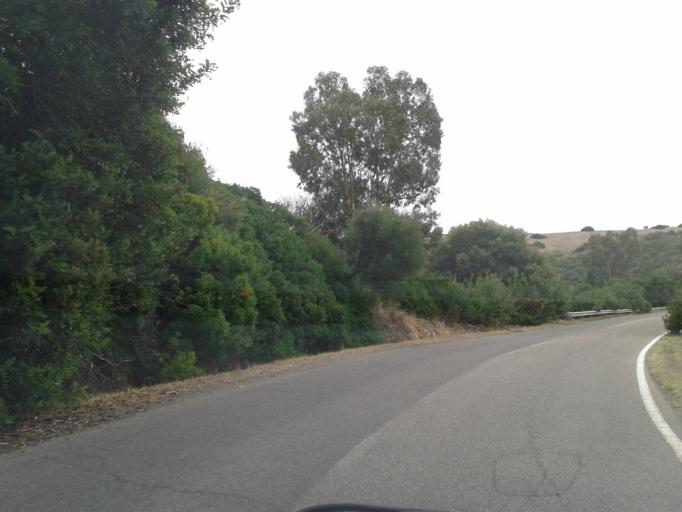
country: IT
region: Sardinia
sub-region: Provincia di Cagliari
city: Olia Speciosa
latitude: 39.2839
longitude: 9.5662
